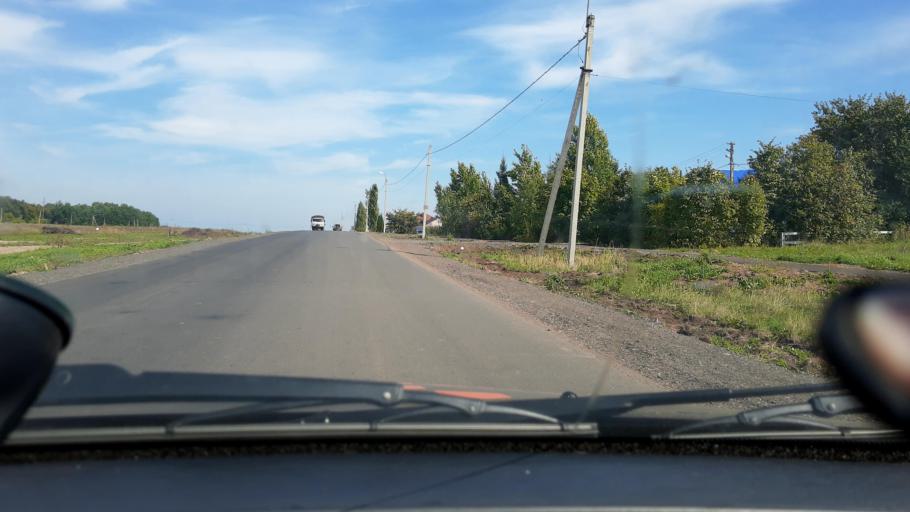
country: RU
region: Bashkortostan
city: Avdon
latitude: 54.6762
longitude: 55.7072
